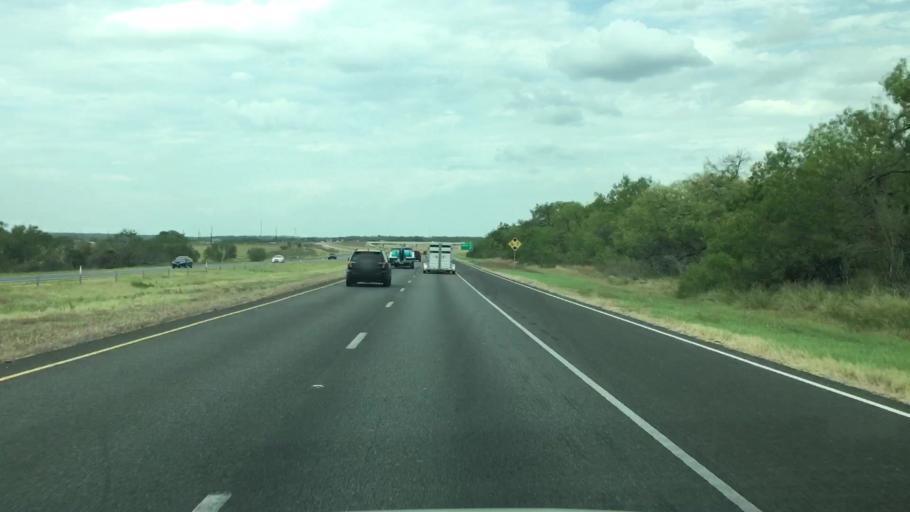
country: US
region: Texas
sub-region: Bexar County
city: Elmendorf
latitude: 29.1346
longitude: -98.4295
